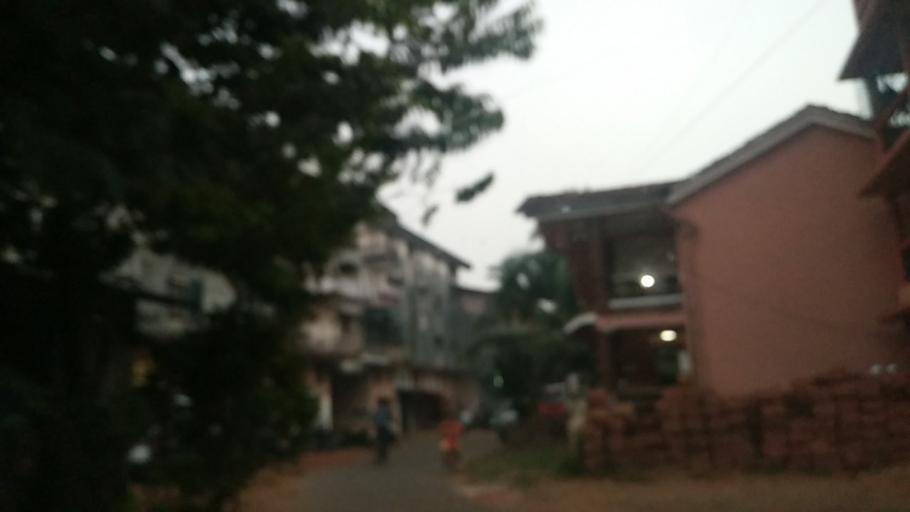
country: IN
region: Goa
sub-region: South Goa
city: Madgaon
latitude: 15.2863
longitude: 73.9548
